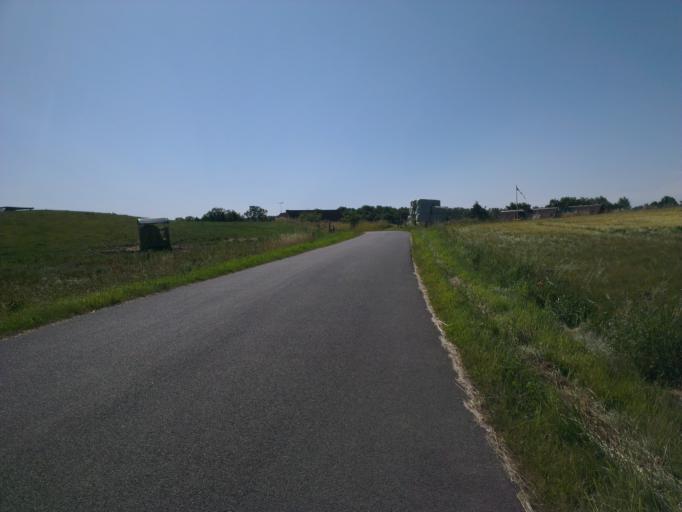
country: DK
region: Zealand
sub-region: Roskilde Kommune
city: Jyllinge
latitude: 55.7680
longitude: 12.0491
